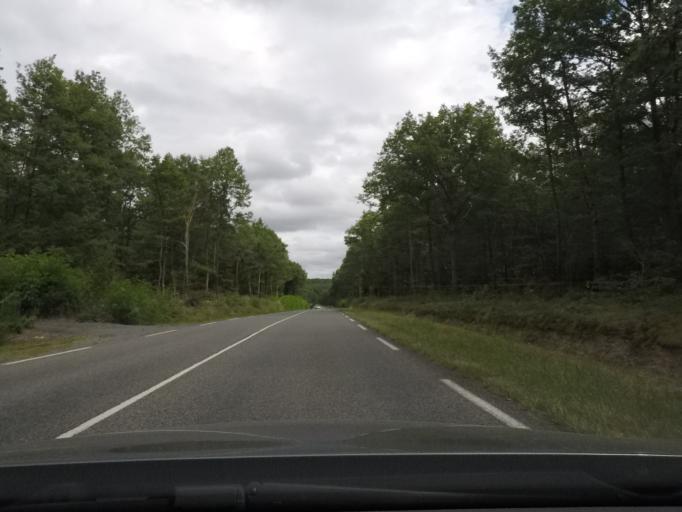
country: FR
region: Auvergne
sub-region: Departement de l'Allier
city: Brugheas
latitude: 46.0600
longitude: 3.3750
